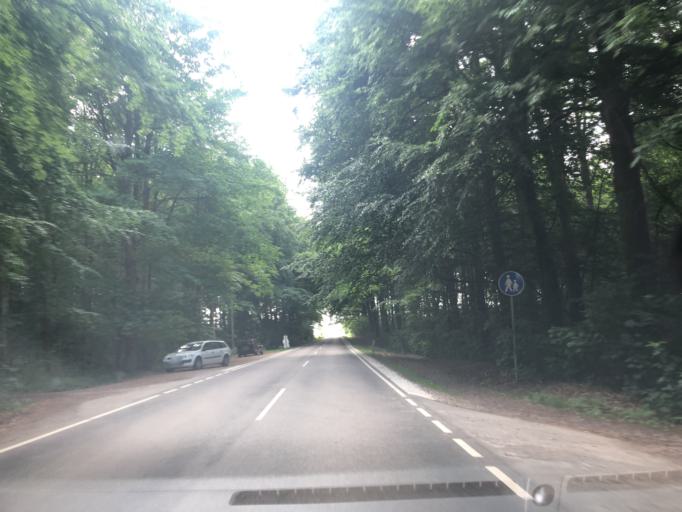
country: DK
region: Zealand
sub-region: Faxe Kommune
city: Haslev
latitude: 55.3116
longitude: 11.9893
